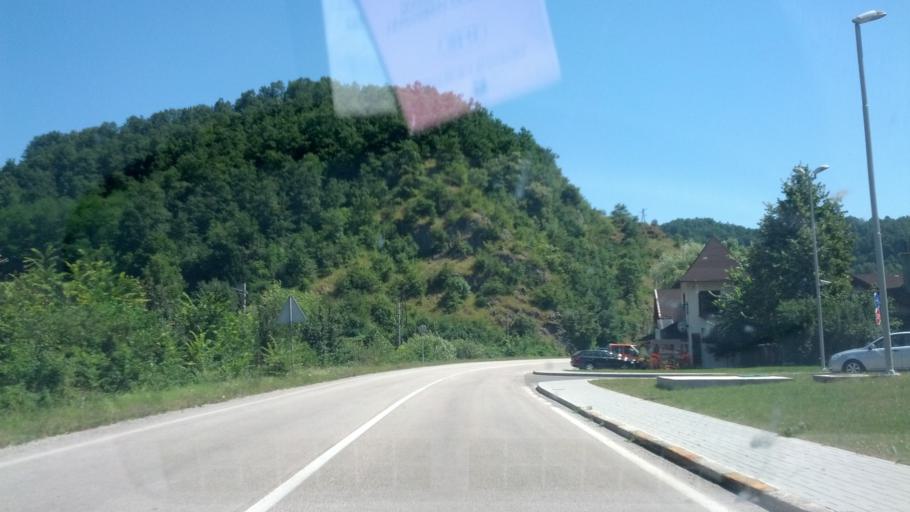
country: BA
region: Federation of Bosnia and Herzegovina
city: Bosanska Krupa
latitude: 44.8995
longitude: 16.1593
